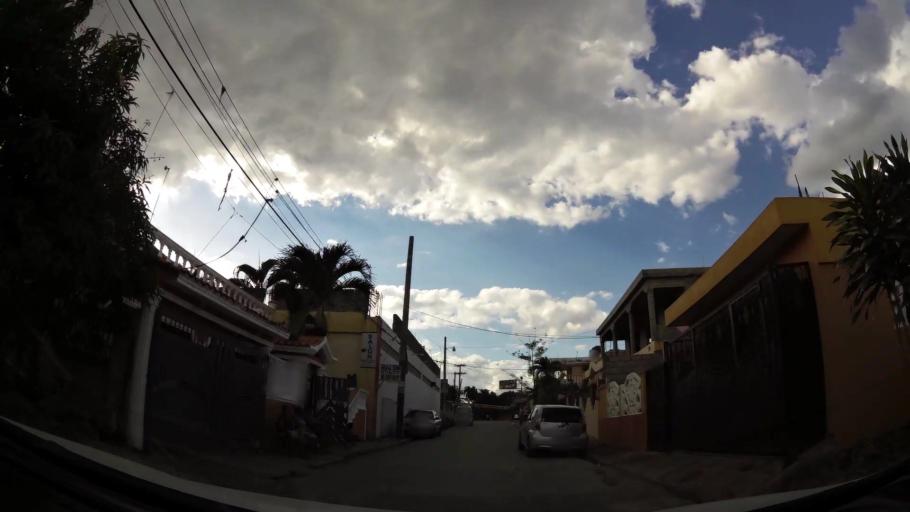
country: DO
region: Nacional
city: Ensanche Luperon
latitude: 18.5615
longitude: -69.9050
